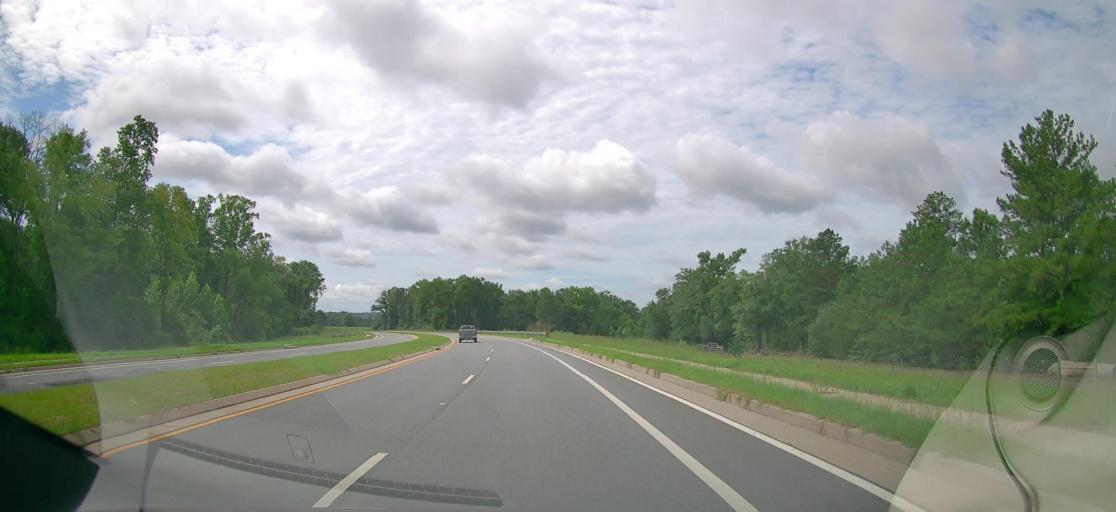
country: US
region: Georgia
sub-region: Houston County
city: Centerville
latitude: 32.7022
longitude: -83.6949
